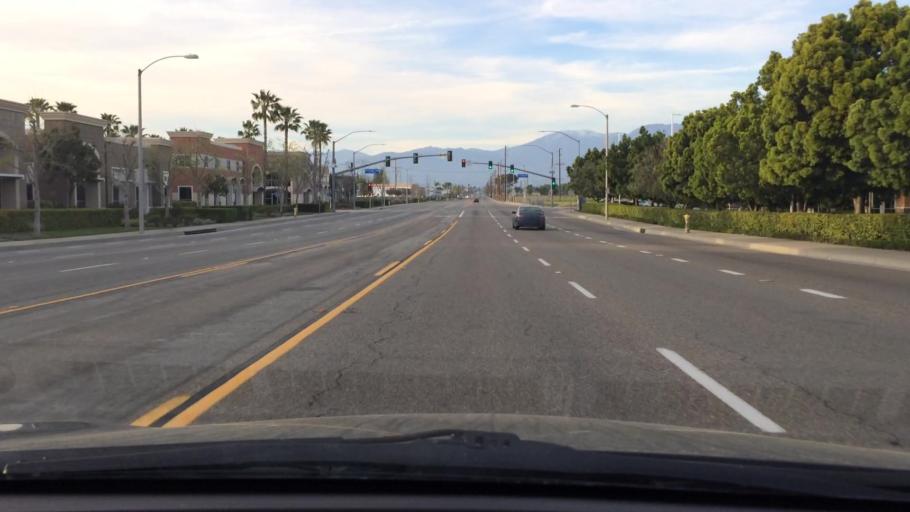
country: US
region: California
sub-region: San Bernardino County
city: Los Serranos
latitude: 33.9752
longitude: -117.6889
